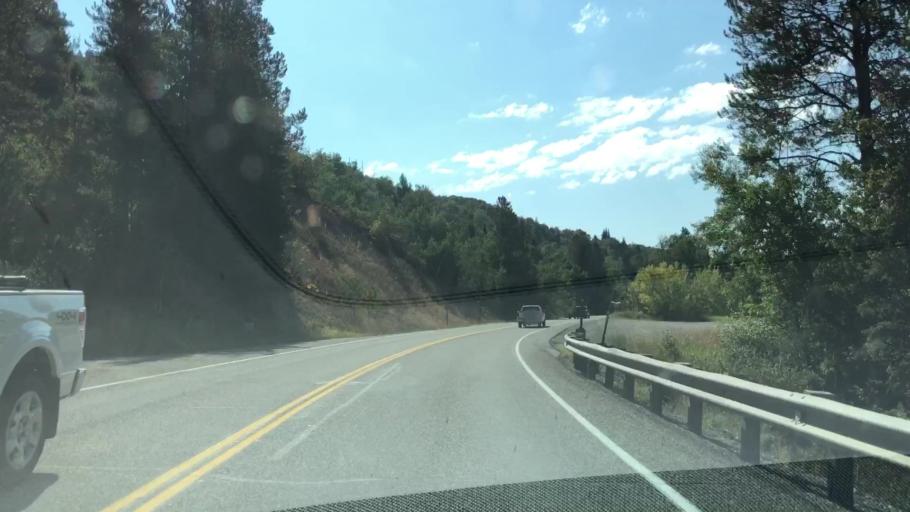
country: US
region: Idaho
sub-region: Teton County
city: Victor
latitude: 43.3250
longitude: -111.1682
